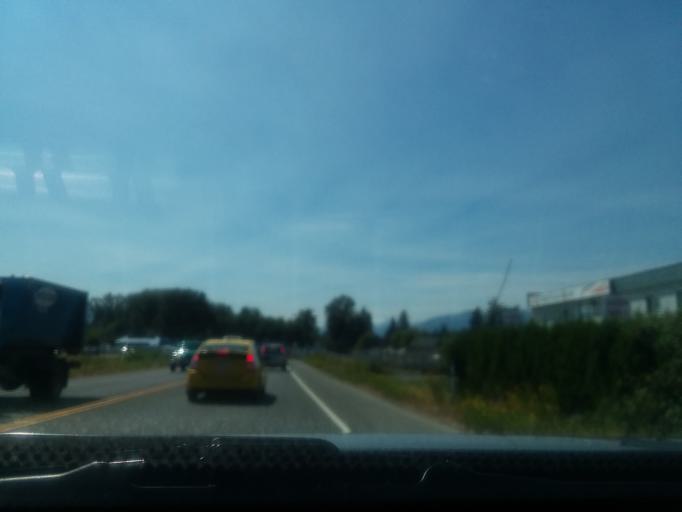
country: CA
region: British Columbia
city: Courtenay
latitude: 49.6945
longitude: -124.9897
